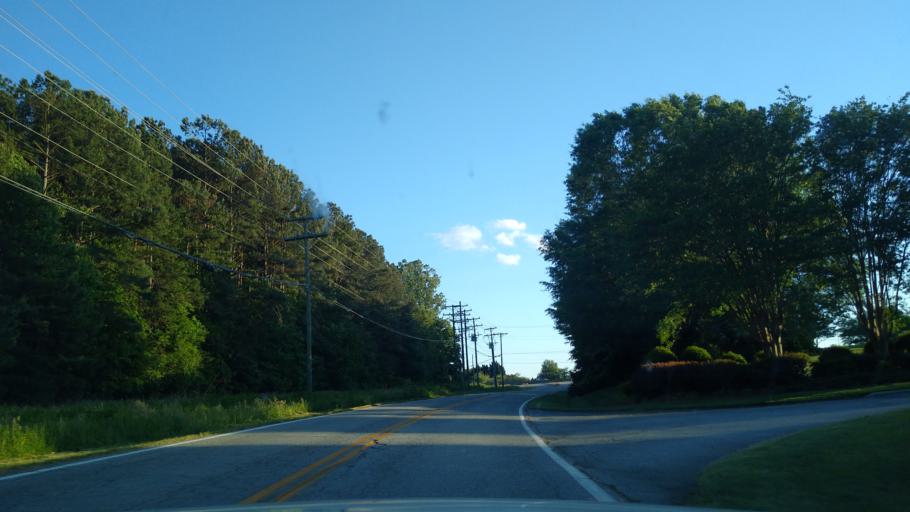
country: US
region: North Carolina
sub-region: Guilford County
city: Oak Ridge
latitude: 36.0860
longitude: -79.9695
